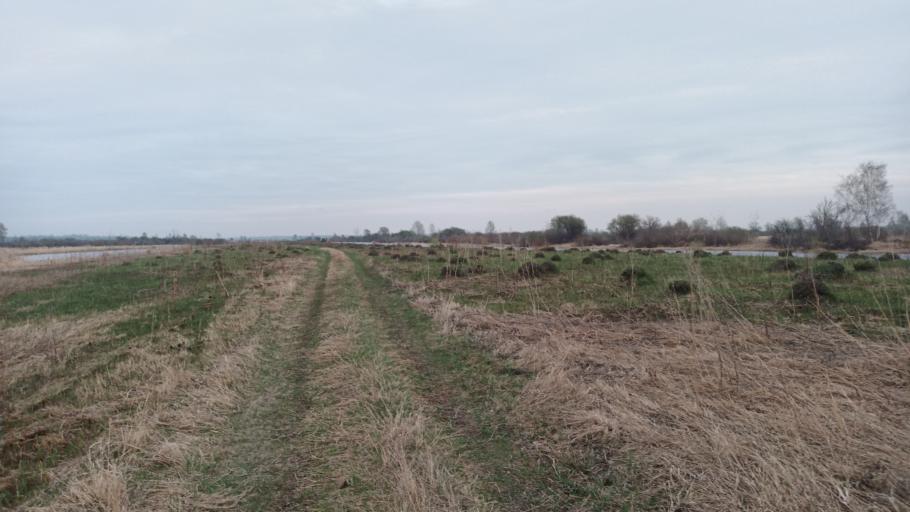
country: RU
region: Altai Krai
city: Yuzhnyy
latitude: 53.2235
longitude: 83.7379
